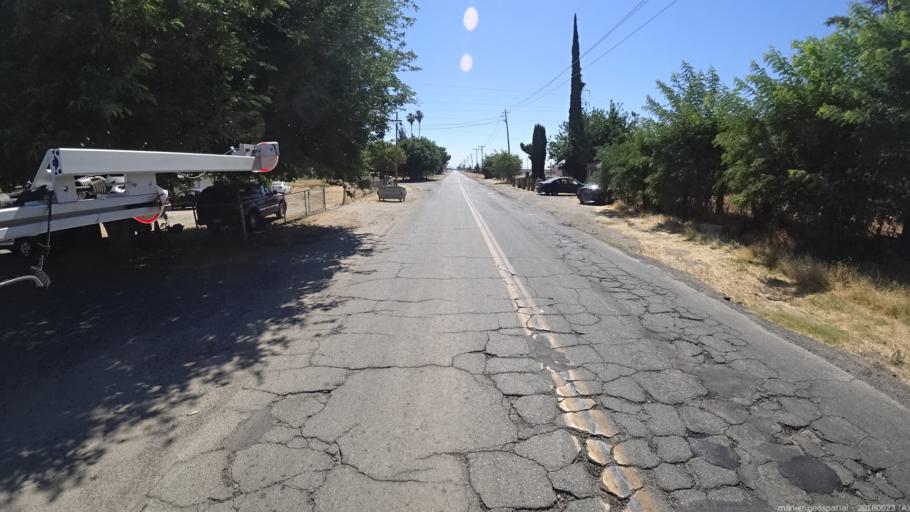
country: US
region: California
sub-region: Madera County
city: Parksdale
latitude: 36.9744
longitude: -120.0271
